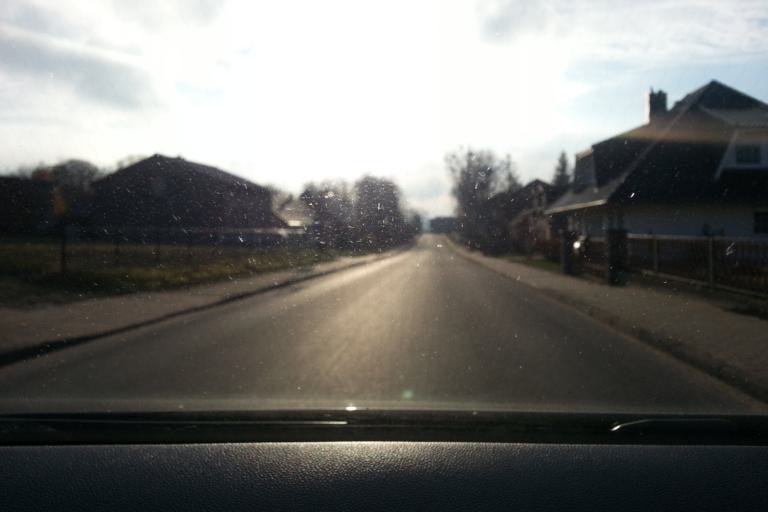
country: DE
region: Mecklenburg-Vorpommern
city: Strasburg
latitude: 53.6154
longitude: 13.7799
